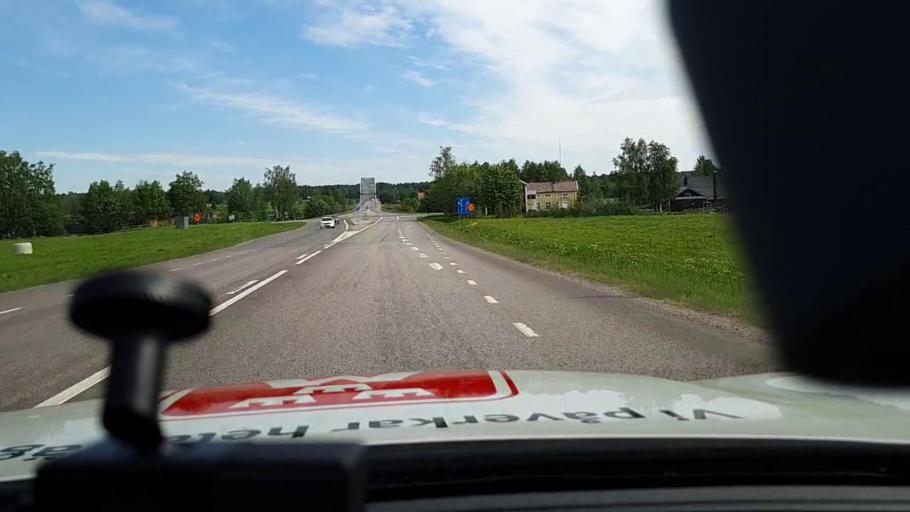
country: SE
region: Norrbotten
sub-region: Lulea Kommun
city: Gammelstad
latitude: 65.5854
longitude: 22.0254
